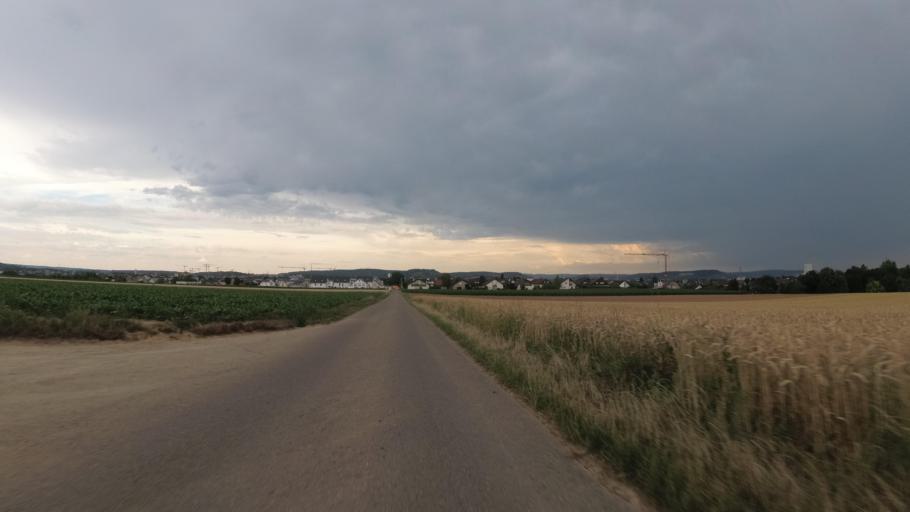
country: DE
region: Baden-Wuerttemberg
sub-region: Regierungsbezirk Stuttgart
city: Untereisesheim
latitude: 49.2128
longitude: 9.1906
